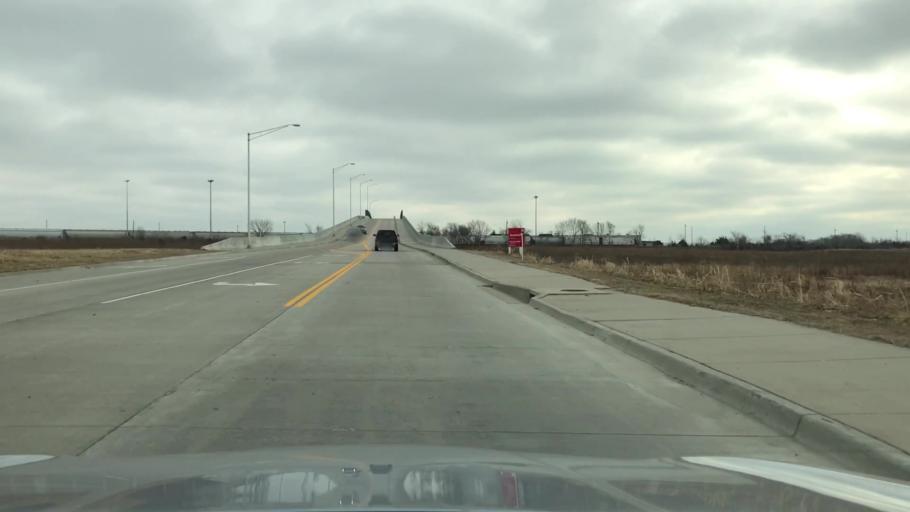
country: US
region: Missouri
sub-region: Jackson County
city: Lees Summit
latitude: 38.8960
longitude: -94.3716
